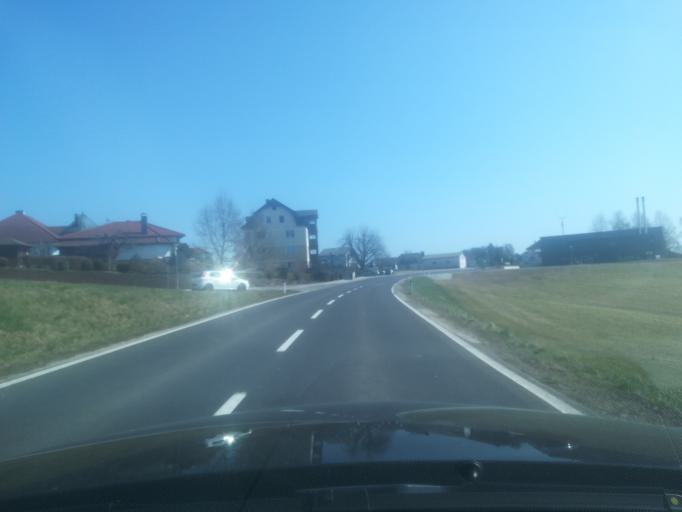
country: AT
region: Upper Austria
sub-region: Politischer Bezirk Freistadt
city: Freistadt
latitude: 48.4199
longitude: 14.6073
